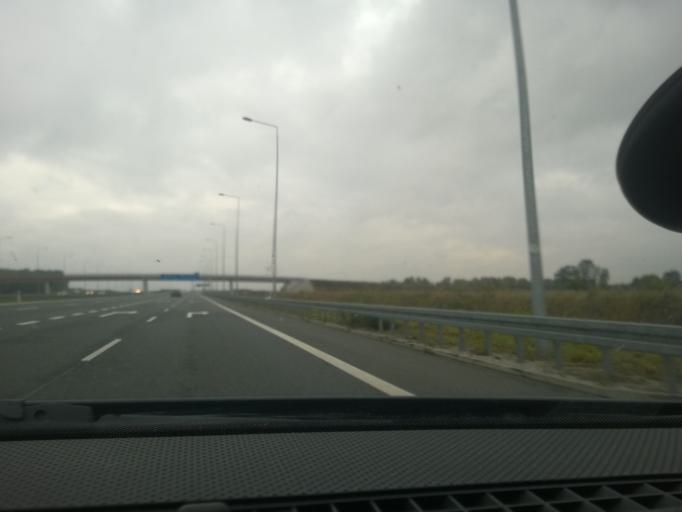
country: PL
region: Lodz Voivodeship
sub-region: Powiat zgierski
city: Strykow
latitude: 51.8823
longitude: 19.6439
